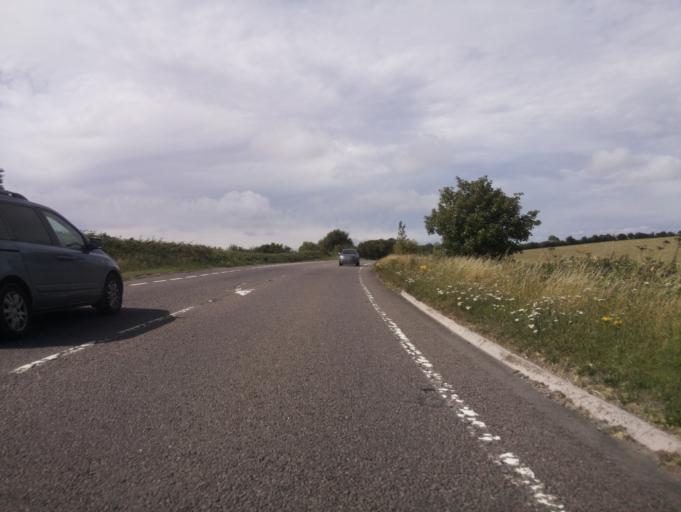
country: GB
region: England
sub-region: Dorset
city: Dorchester
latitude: 50.7721
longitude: -2.5387
